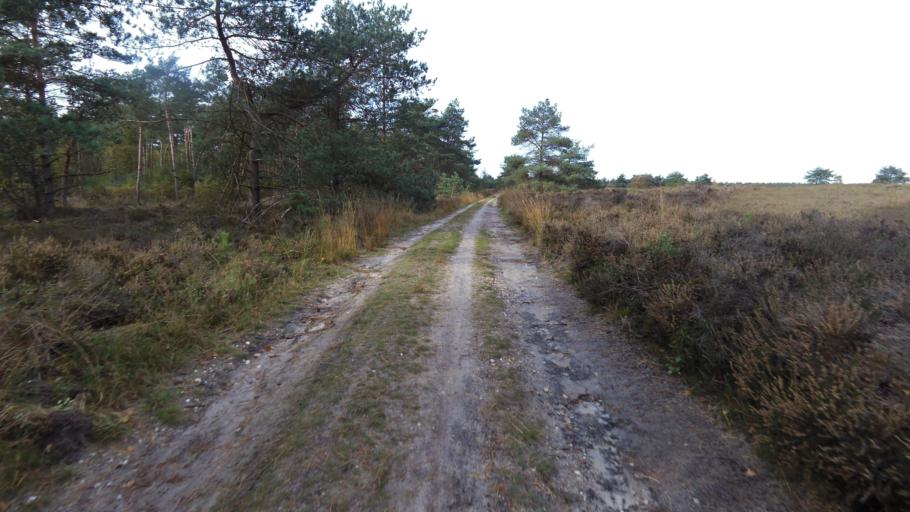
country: NL
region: Gelderland
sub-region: Gemeente Epe
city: Emst
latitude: 52.3232
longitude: 5.8822
